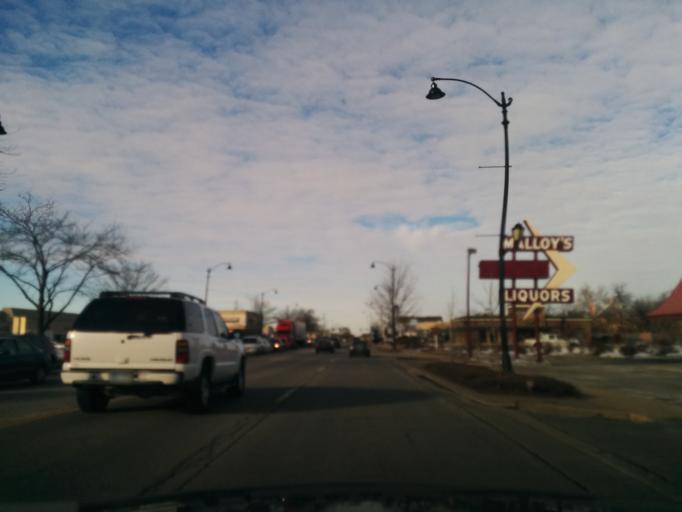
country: US
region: Illinois
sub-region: DuPage County
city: Glen Ellyn
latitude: 41.8594
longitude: -88.0636
